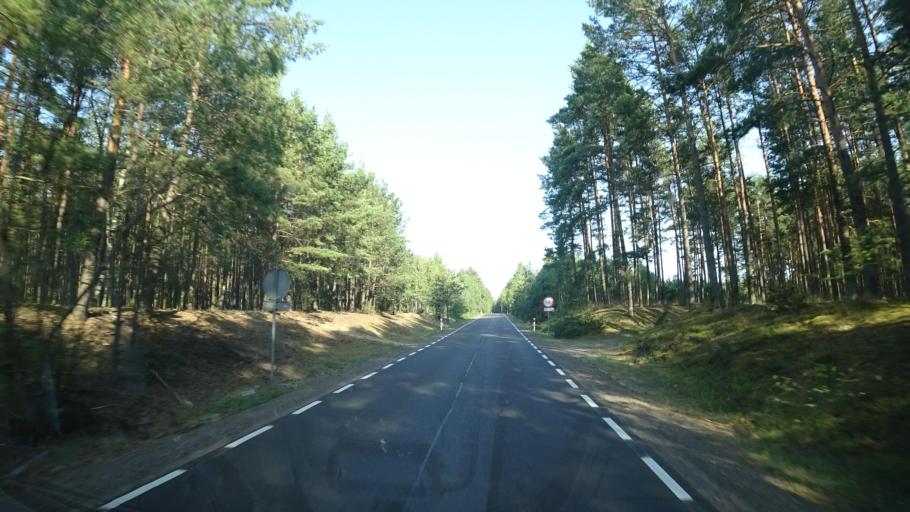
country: PL
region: Pomeranian Voivodeship
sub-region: Powiat chojnicki
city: Chojnice
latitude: 53.8617
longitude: 17.5242
